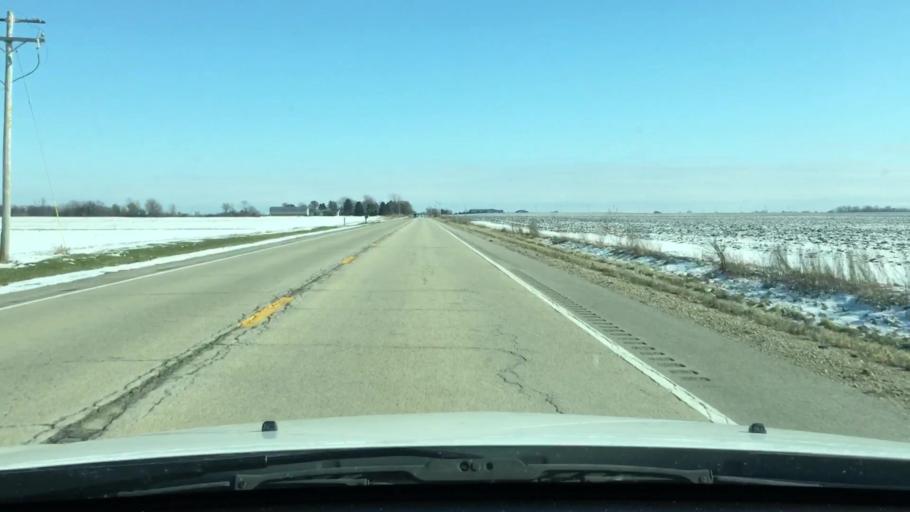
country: US
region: Illinois
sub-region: DeKalb County
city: DeKalb
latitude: 42.0015
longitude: -88.7992
